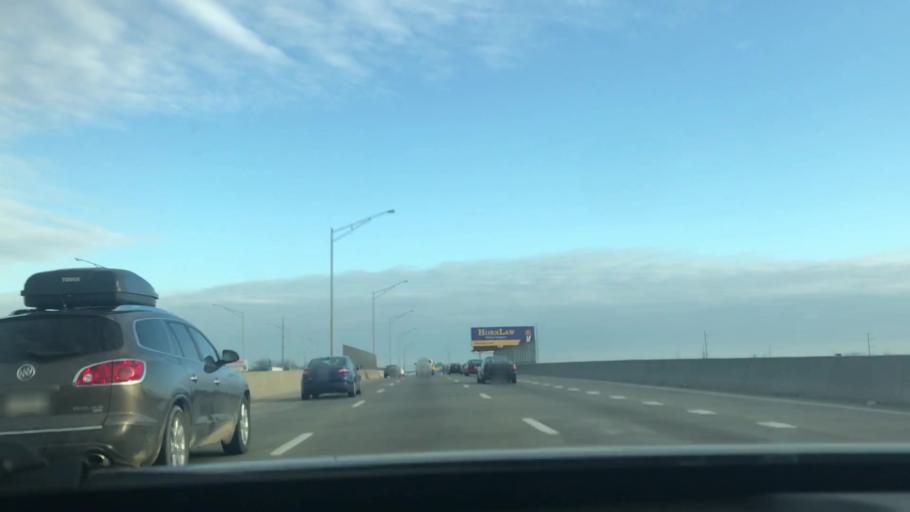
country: US
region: Missouri
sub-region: Jackson County
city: Raytown
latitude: 39.0654
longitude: -94.5042
